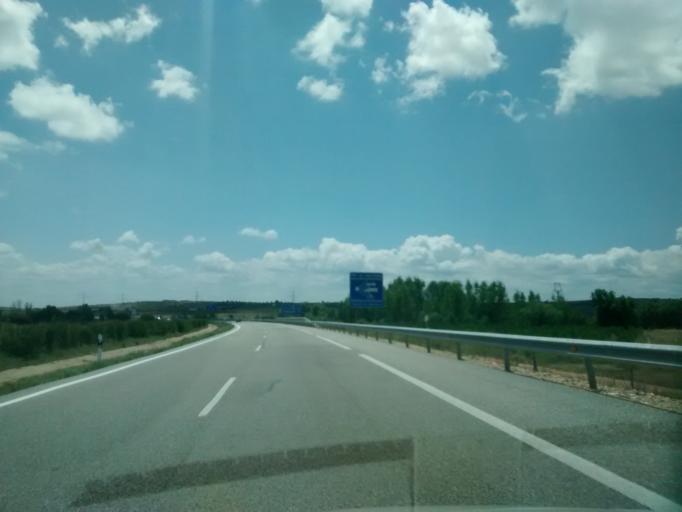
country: ES
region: Castille and Leon
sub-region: Provincia de Leon
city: Astorga
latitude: 42.4573
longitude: -6.0846
